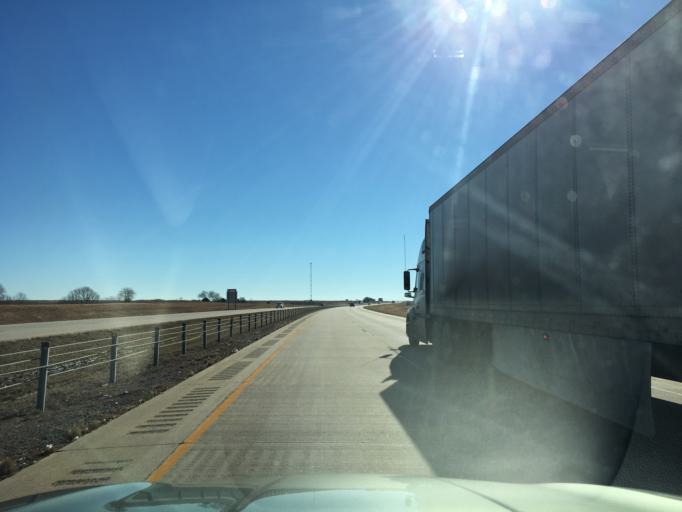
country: US
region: Oklahoma
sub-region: Kay County
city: Tonkawa
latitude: 36.5220
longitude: -97.3385
